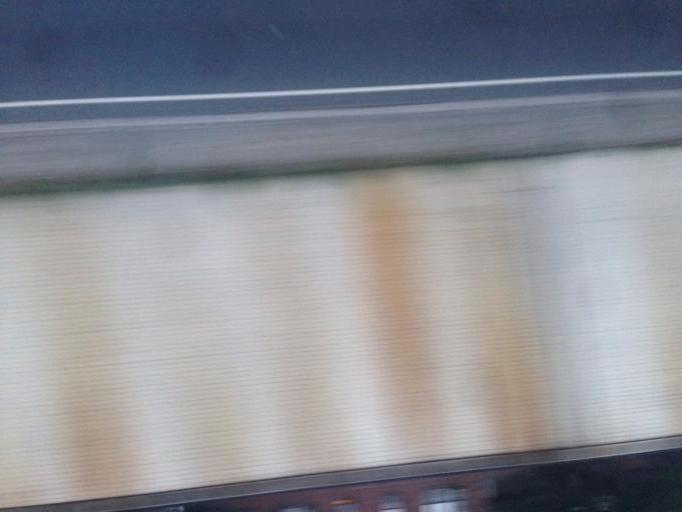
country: US
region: New York
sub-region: Kings County
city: Brooklyn
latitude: 40.6469
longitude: -73.9747
